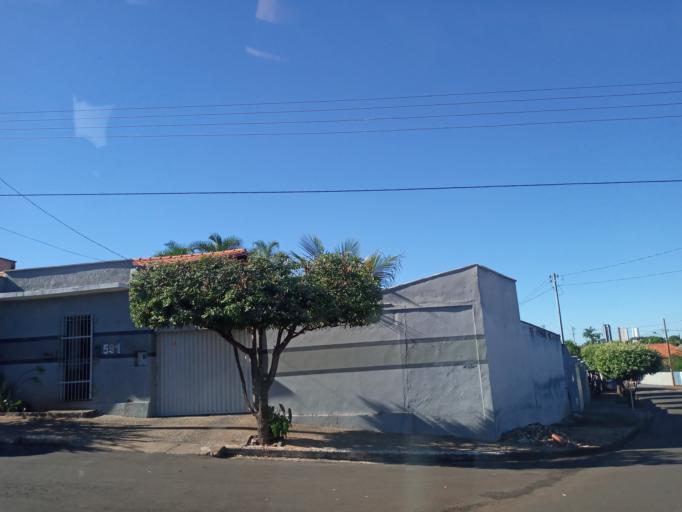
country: BR
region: Minas Gerais
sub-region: Ituiutaba
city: Ituiutaba
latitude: -18.9798
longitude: -49.4749
